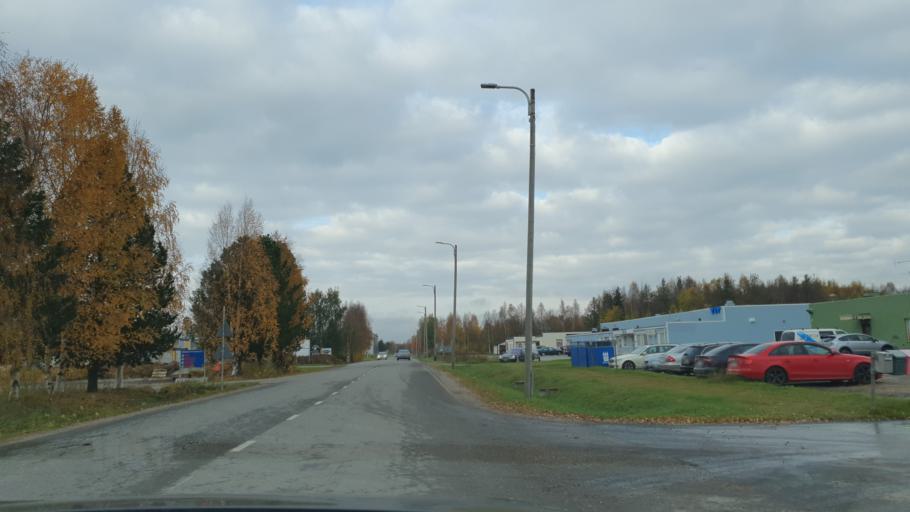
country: FI
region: Lapland
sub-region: Rovaniemi
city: Rovaniemi
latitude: 66.4921
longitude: 25.6704
